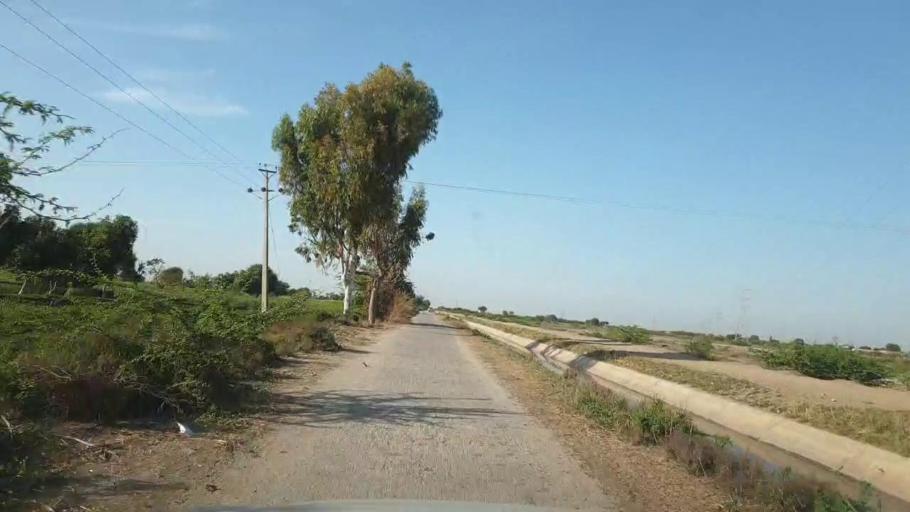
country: PK
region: Sindh
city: Kunri
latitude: 25.0885
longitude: 69.4293
